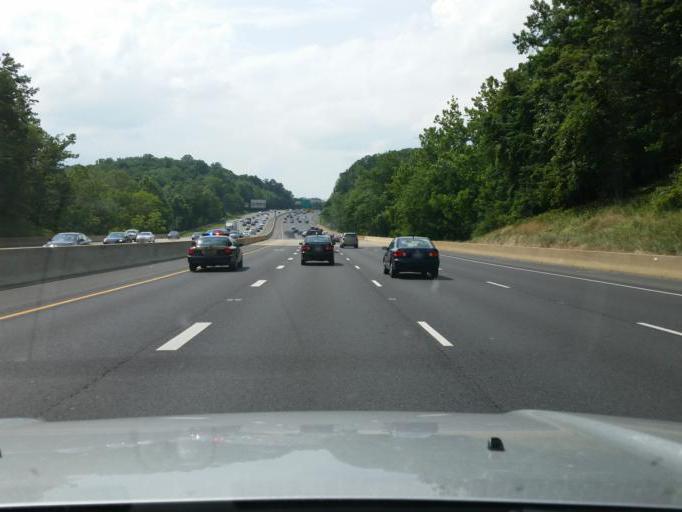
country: US
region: Maryland
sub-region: Montgomery County
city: Gaithersburg
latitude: 39.1603
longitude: -77.2311
